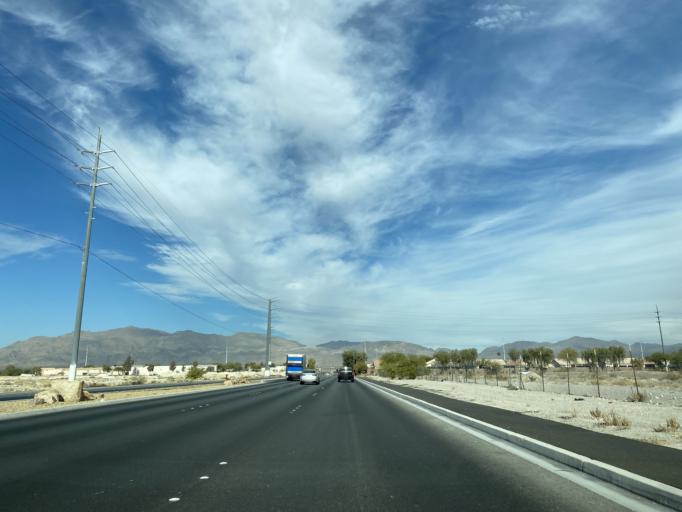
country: US
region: Nevada
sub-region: Clark County
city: Nellis Air Force Base
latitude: 36.2708
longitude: -115.1169
